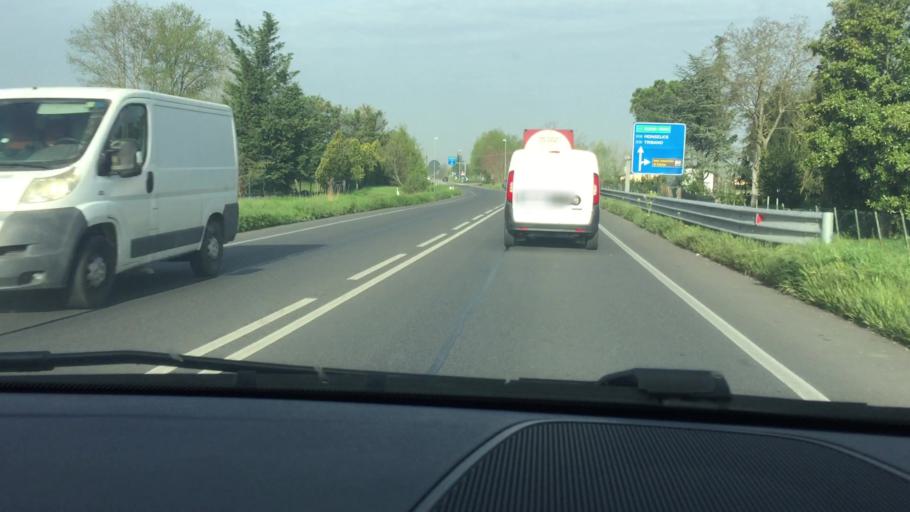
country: IT
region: Veneto
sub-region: Provincia di Padova
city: Tribano
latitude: 45.2154
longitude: 11.8505
